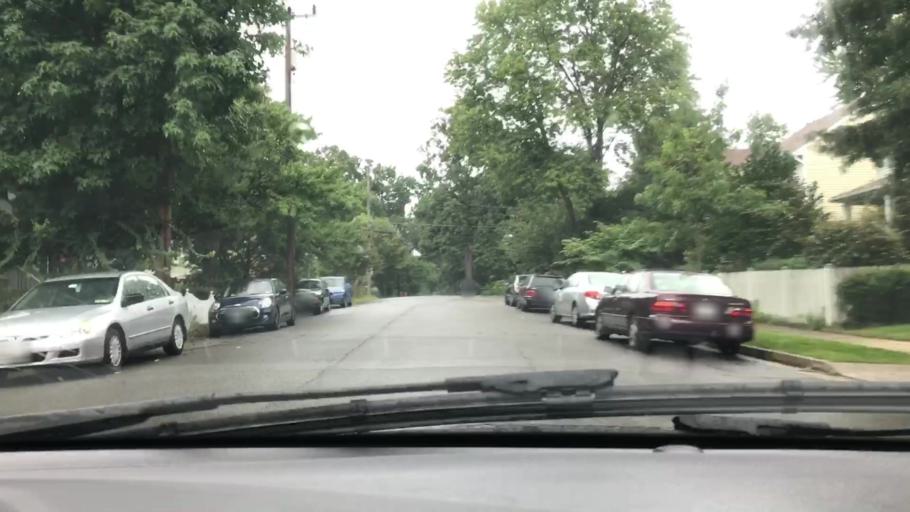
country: US
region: Virginia
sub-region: Arlington County
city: Arlington
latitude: 38.8738
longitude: -77.0923
